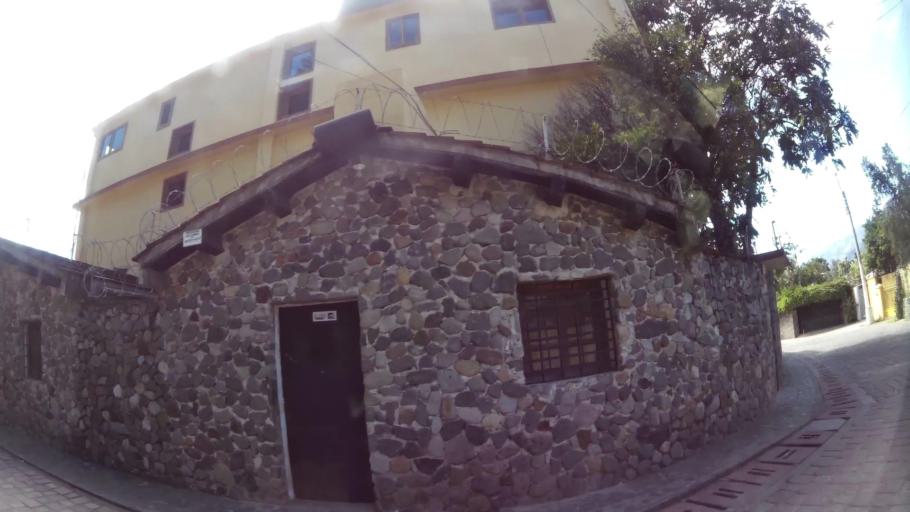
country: GT
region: Solola
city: Panajachel
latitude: 14.7411
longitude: -91.1606
